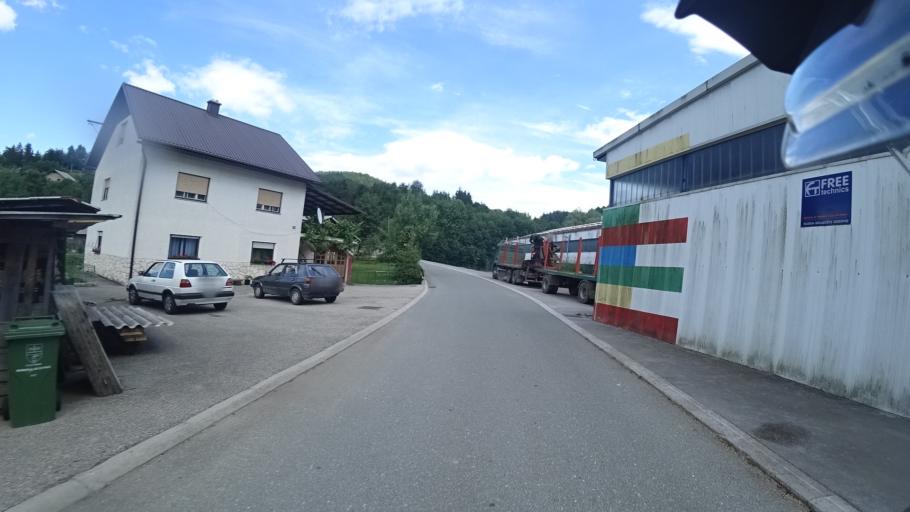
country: SI
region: Osilnica
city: Osilnica
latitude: 45.5147
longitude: 14.6458
